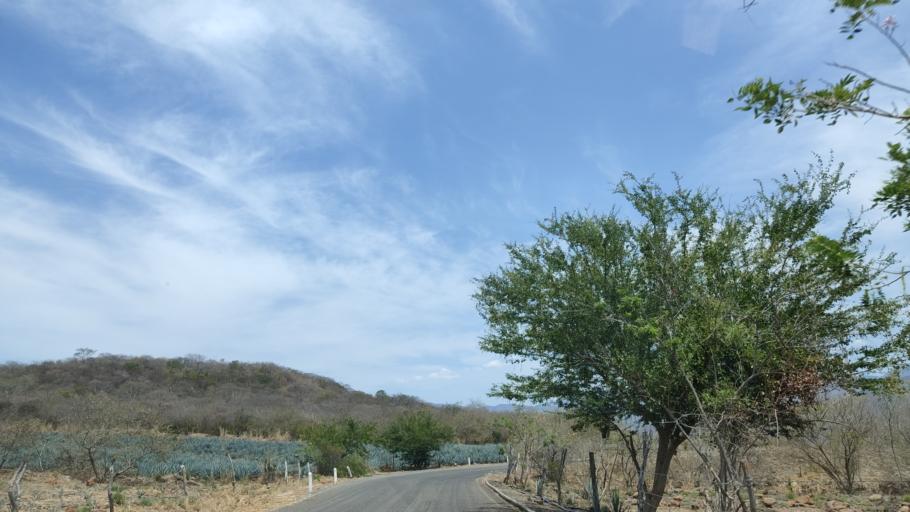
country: MX
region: Nayarit
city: Santa Maria del Oro
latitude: 21.5092
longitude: -104.5992
